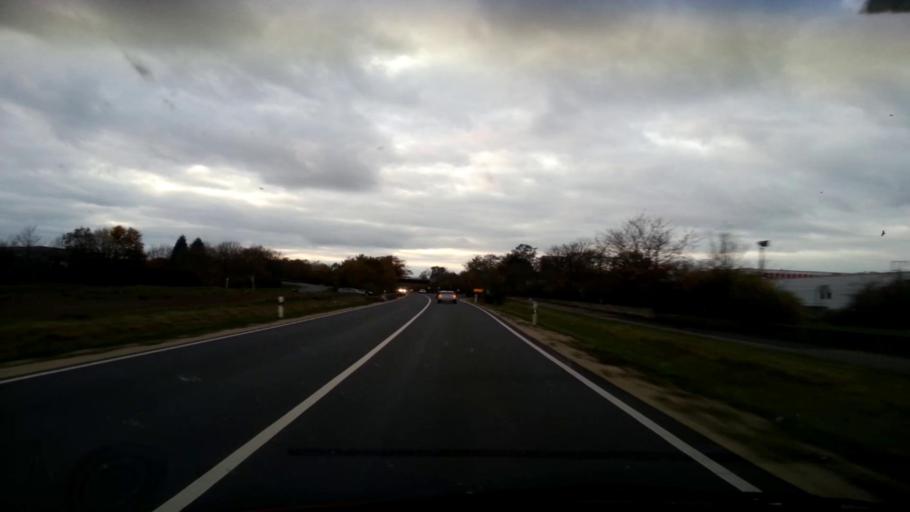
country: DE
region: Bavaria
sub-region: Upper Franconia
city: Sonnefeld
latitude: 50.2138
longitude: 11.0806
